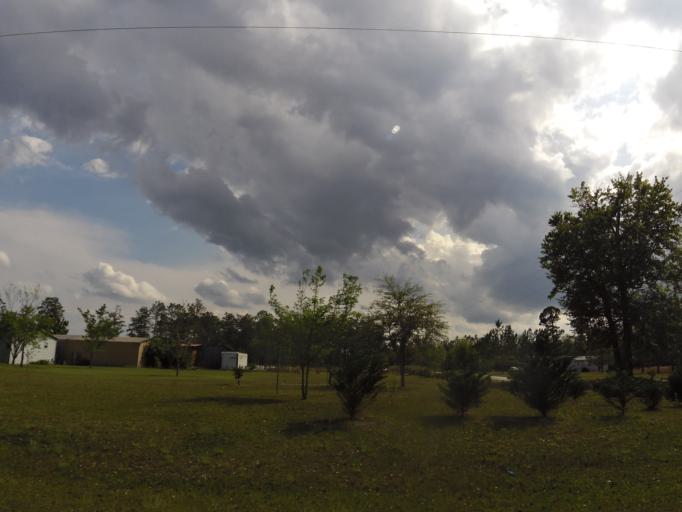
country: US
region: Georgia
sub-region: Charlton County
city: Folkston
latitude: 30.8061
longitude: -82.0406
